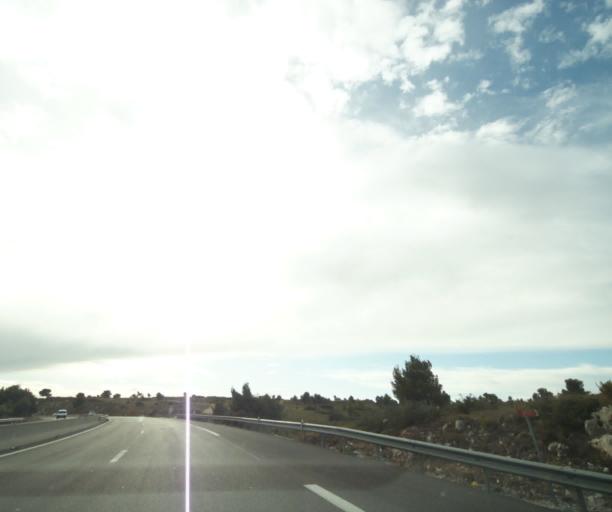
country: FR
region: Provence-Alpes-Cote d'Azur
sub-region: Departement des Bouches-du-Rhone
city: Carry-le-Rouet
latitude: 43.3523
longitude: 5.1710
